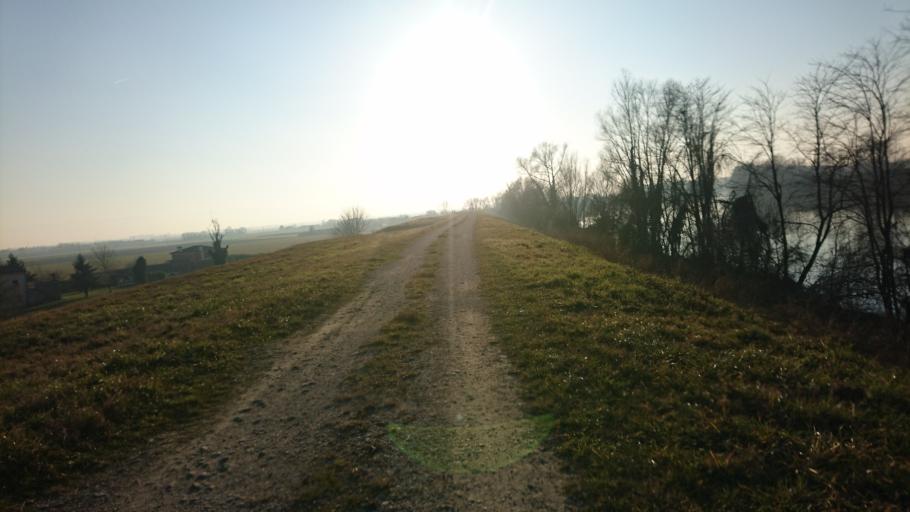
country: IT
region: Veneto
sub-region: Provincia di Rovigo
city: Mardimago
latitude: 45.1241
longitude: 11.8365
